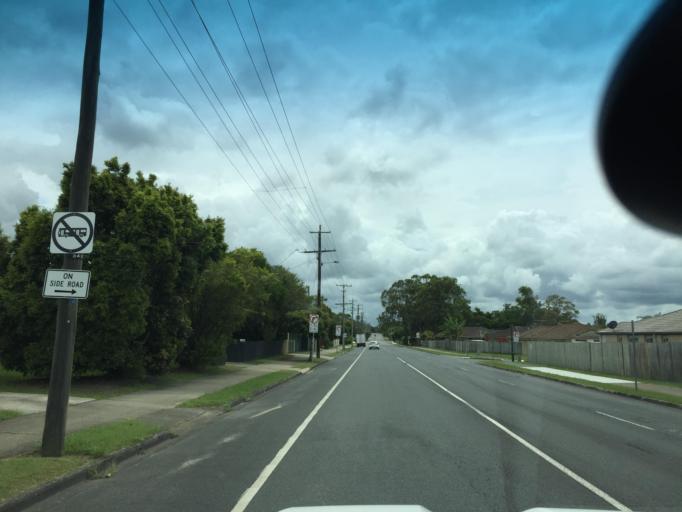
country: AU
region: Queensland
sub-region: Moreton Bay
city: Caboolture
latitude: -27.0756
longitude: 152.9321
